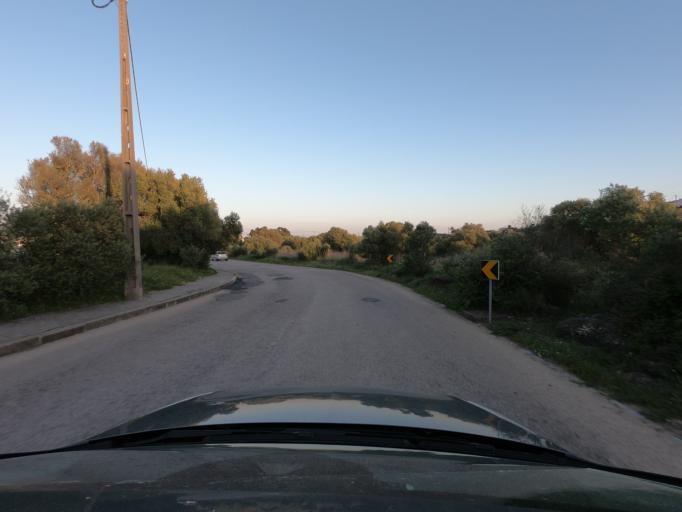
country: PT
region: Lisbon
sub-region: Sintra
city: Rio de Mouro
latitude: 38.7519
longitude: -9.3555
